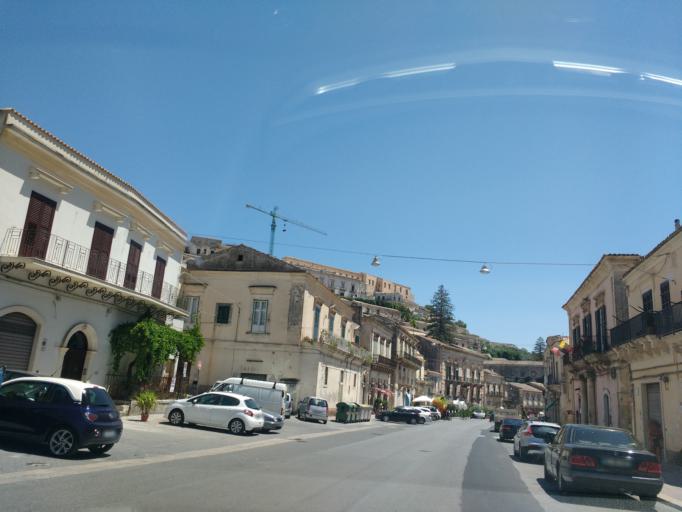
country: IT
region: Sicily
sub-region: Ragusa
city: Modica
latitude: 36.8643
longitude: 14.7592
